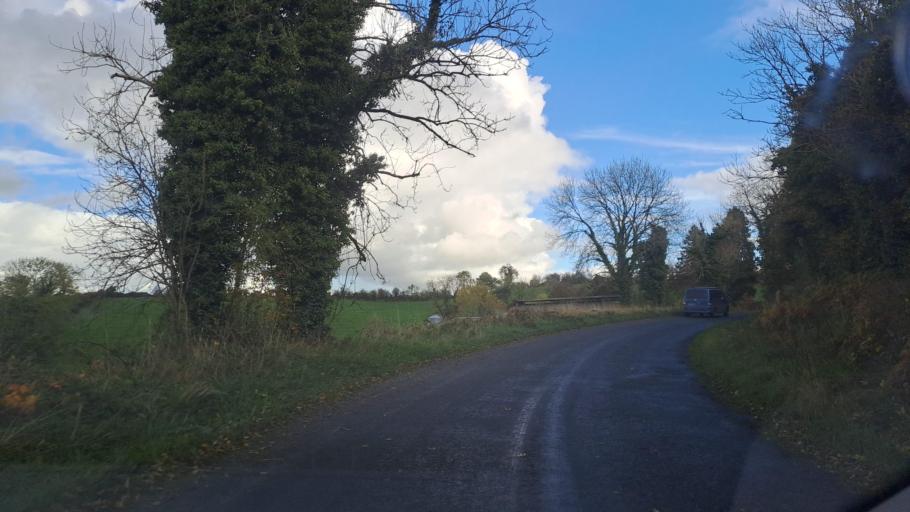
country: IE
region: Ulster
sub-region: An Cabhan
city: Bailieborough
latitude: 53.9967
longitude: -6.9612
